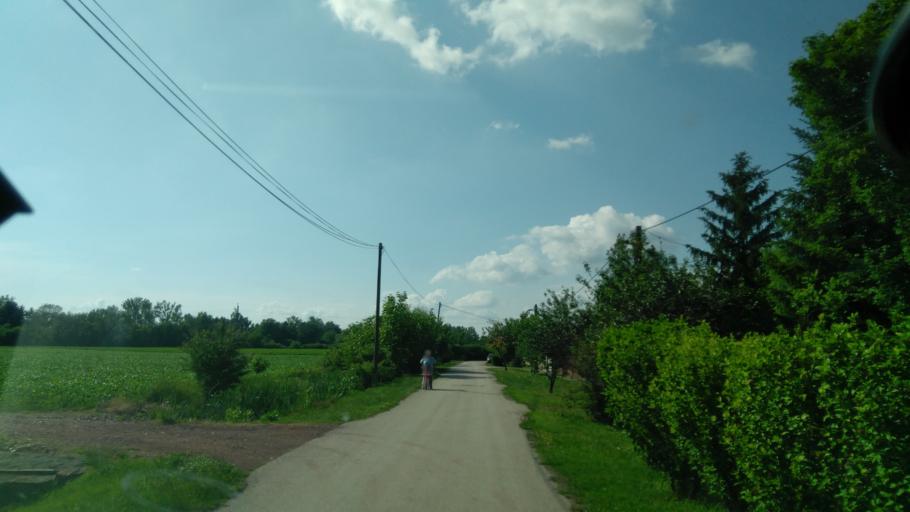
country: HU
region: Bekes
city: Bekes
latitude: 46.7038
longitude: 21.1764
